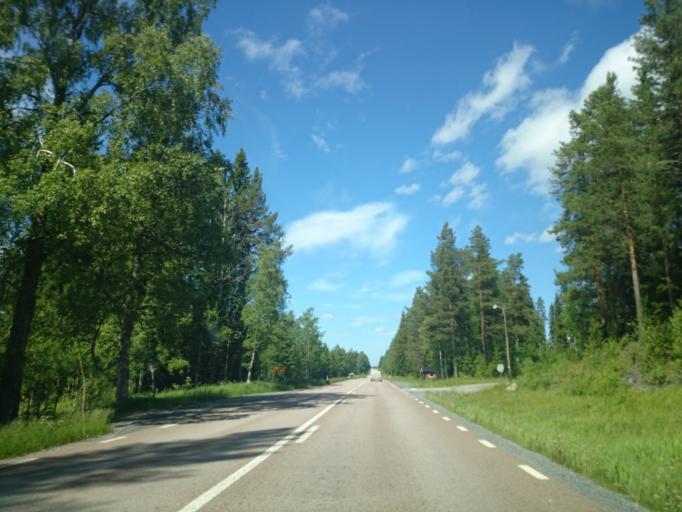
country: SE
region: Jaemtland
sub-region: OEstersunds Kommun
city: Brunflo
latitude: 62.9797
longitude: 15.0035
